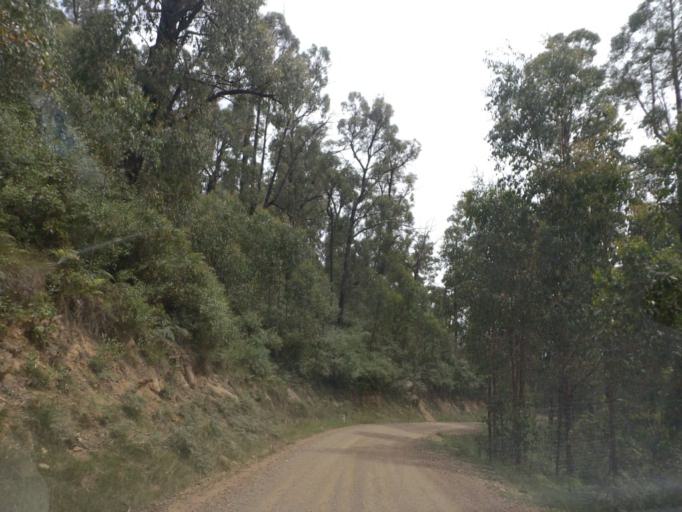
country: AU
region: Victoria
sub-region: Yarra Ranges
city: Healesville
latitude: -37.4472
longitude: 145.5779
